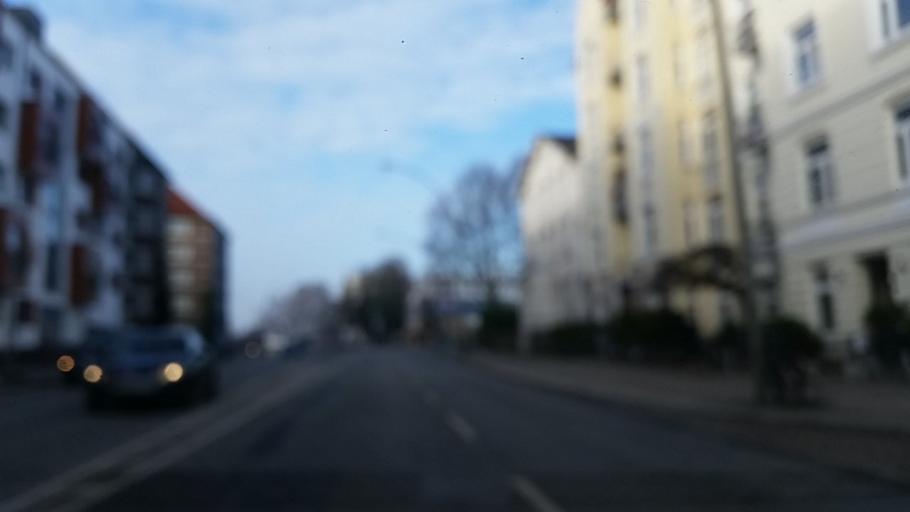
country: DE
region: Hamburg
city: Hamburg-Nord
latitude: 53.5973
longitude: 9.9794
